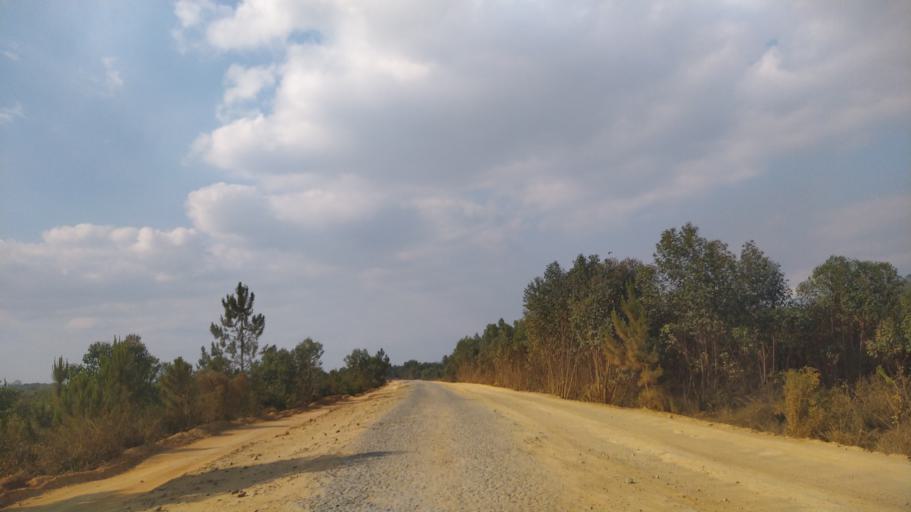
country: MG
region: Alaotra Mangoro
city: Moramanga
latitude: -18.6462
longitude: 48.2751
